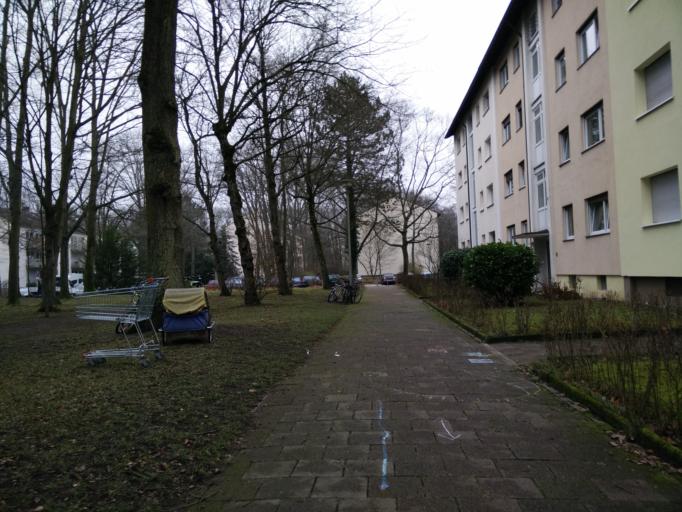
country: DE
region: Baden-Wuerttemberg
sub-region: Karlsruhe Region
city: Karlsruhe
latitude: 49.0370
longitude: 8.4422
